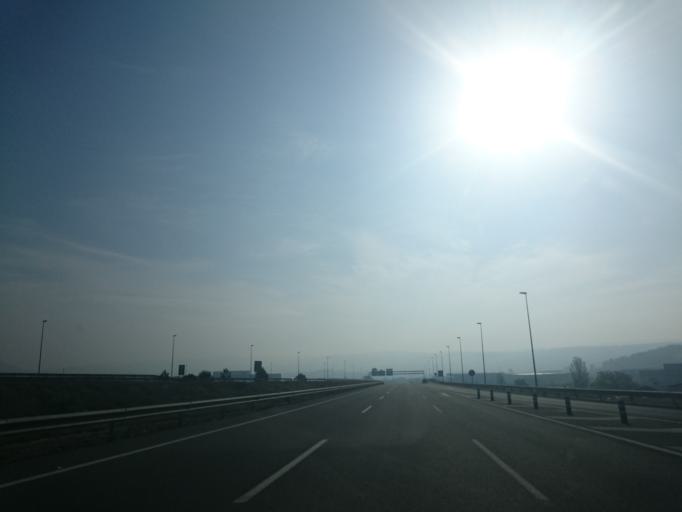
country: ES
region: Catalonia
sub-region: Provincia de Barcelona
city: Navarcles
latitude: 41.7793
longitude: 1.8882
